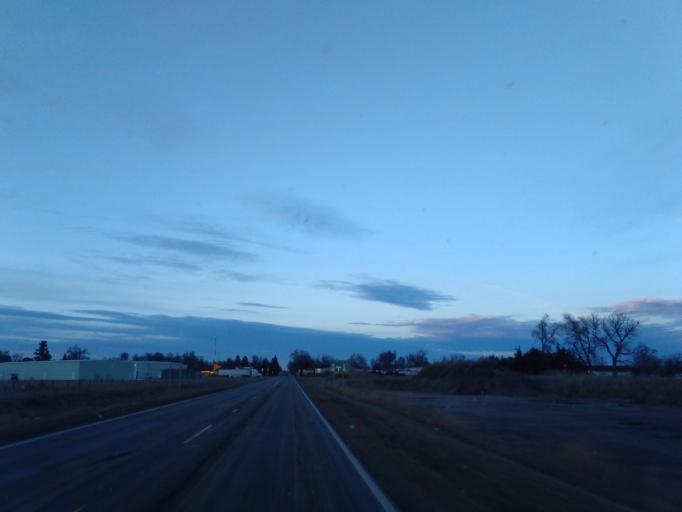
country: US
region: Nebraska
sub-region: Garden County
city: Oshkosh
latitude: 41.3989
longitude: -102.3475
